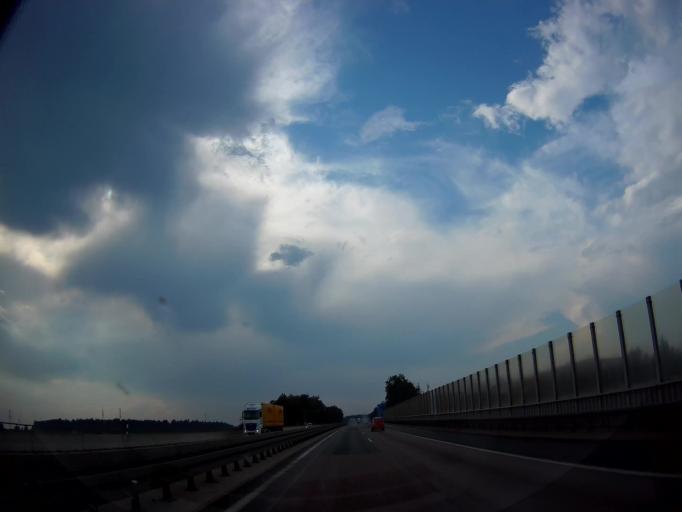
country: DE
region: Bavaria
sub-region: Regierungsbezirk Mittelfranken
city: Altdorf
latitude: 49.3795
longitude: 11.3495
